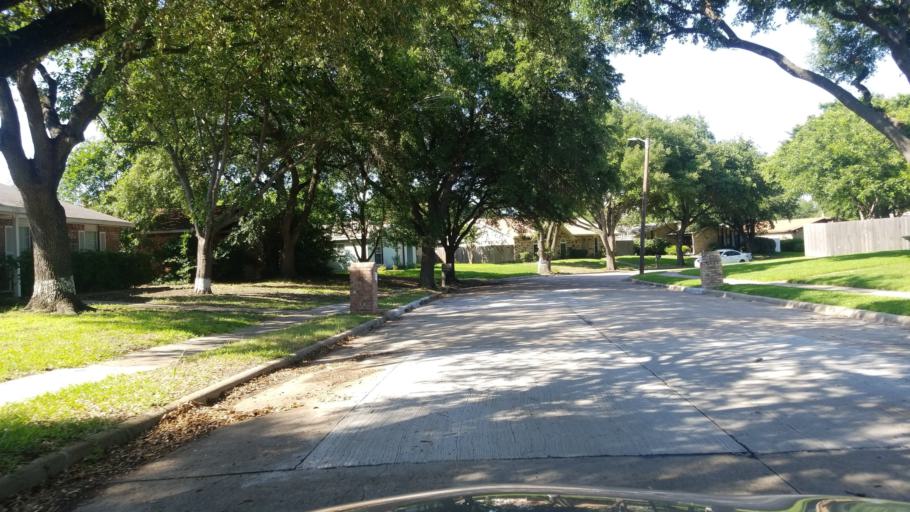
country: US
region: Texas
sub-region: Dallas County
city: Grand Prairie
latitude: 32.6812
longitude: -97.0159
